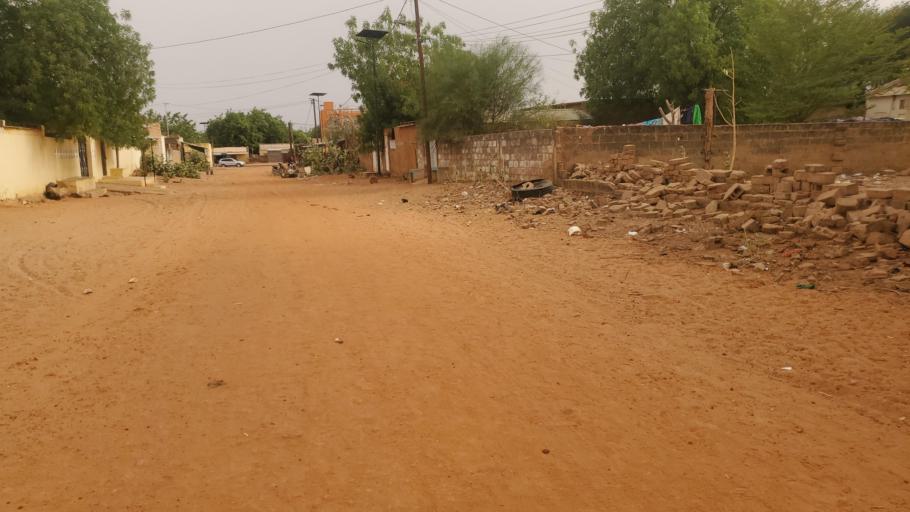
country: SN
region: Louga
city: Ndibene Dahra
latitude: 15.3975
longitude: -15.1184
